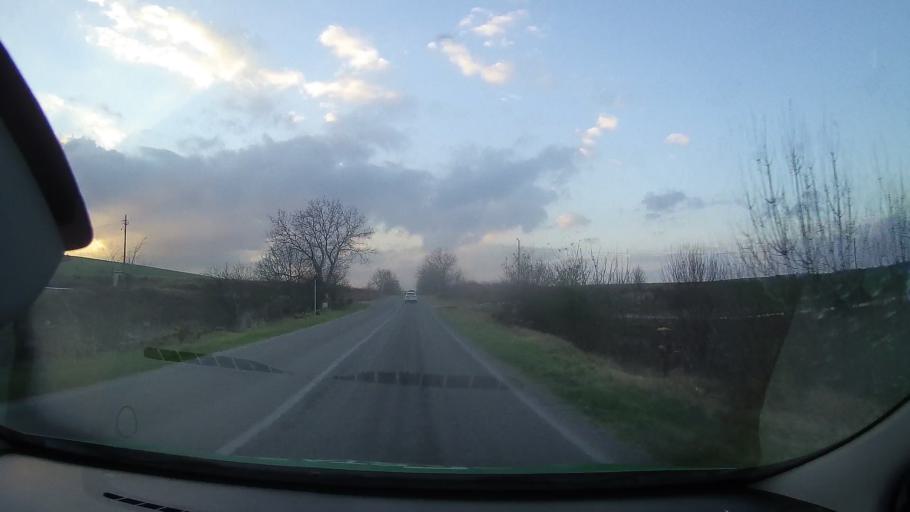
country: RO
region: Constanta
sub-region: Comuna Lipnita
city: Lipnita
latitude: 44.0944
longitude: 27.6413
